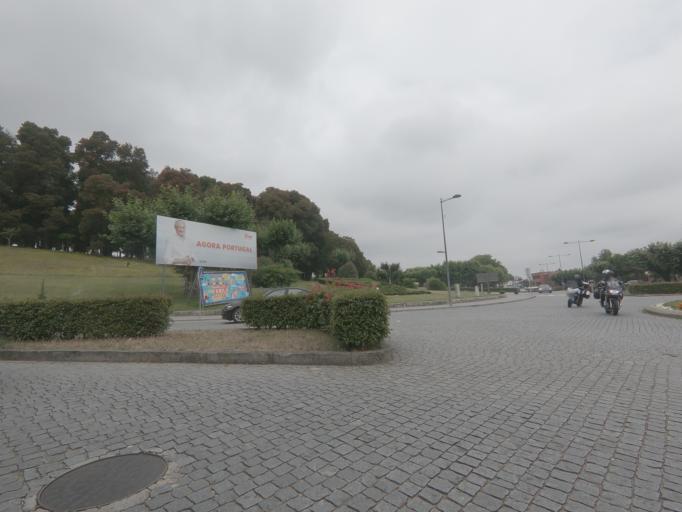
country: PT
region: Viana do Castelo
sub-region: Valenca
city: Valenca
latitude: 42.0267
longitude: -8.6424
